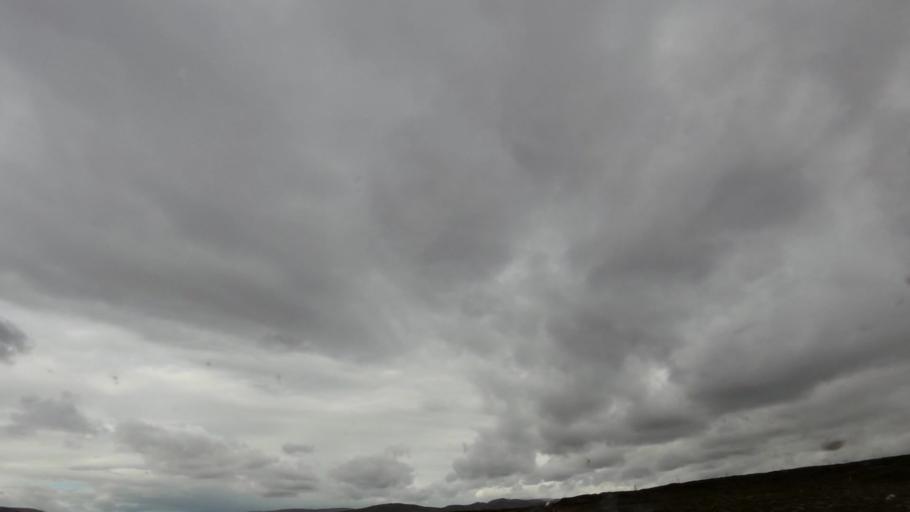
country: IS
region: West
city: Borgarnes
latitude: 65.1818
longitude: -21.7165
